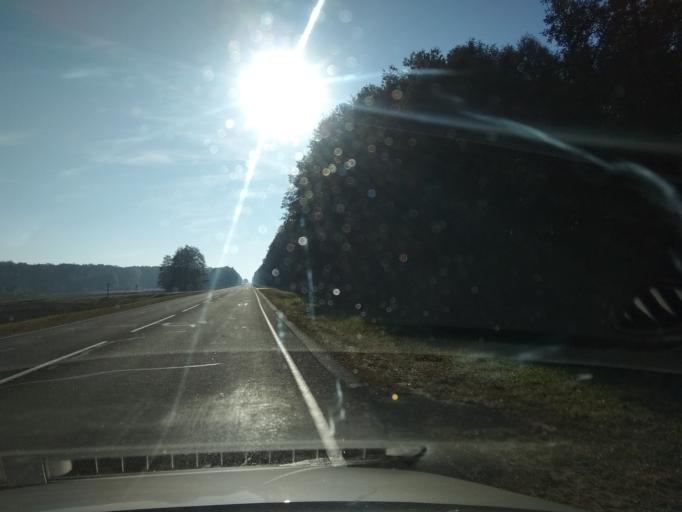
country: BY
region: Brest
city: Malaryta
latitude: 51.8796
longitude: 24.1648
